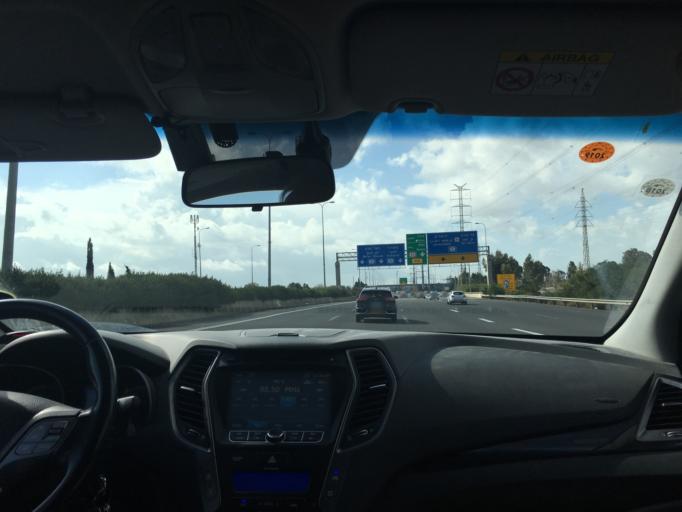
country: IL
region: Tel Aviv
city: Azor
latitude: 32.0283
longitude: 34.8282
